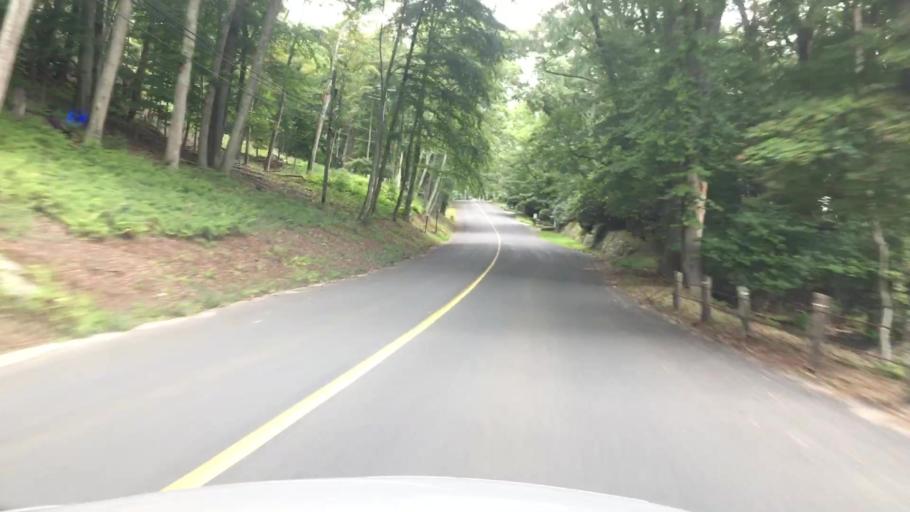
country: US
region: Connecticut
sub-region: Middlesex County
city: Essex Village
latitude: 41.3751
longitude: -72.3880
